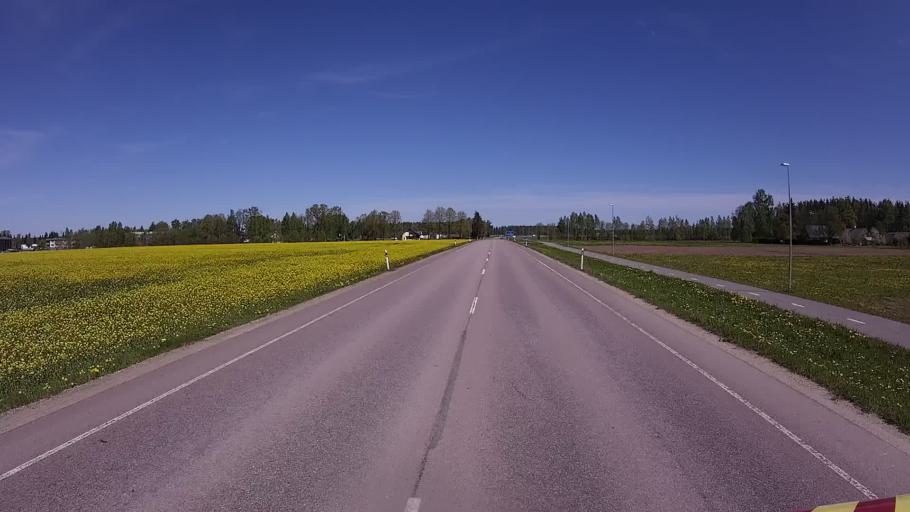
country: EE
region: Polvamaa
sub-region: Polva linn
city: Polva
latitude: 58.0829
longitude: 27.0904
